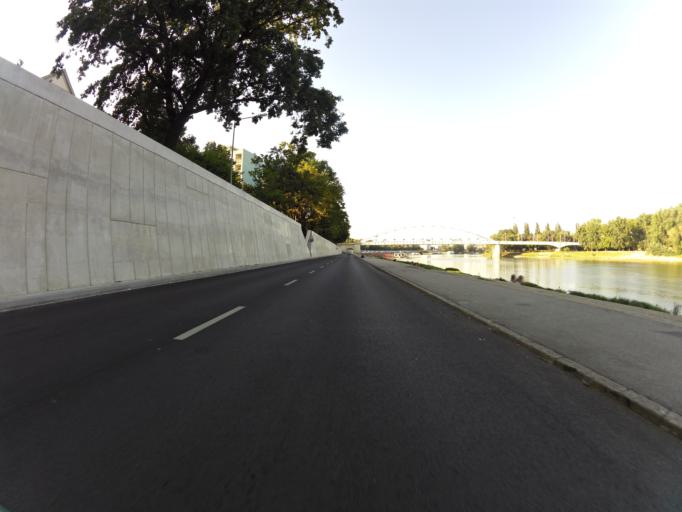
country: HU
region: Csongrad
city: Szeged
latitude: 46.2479
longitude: 20.1513
